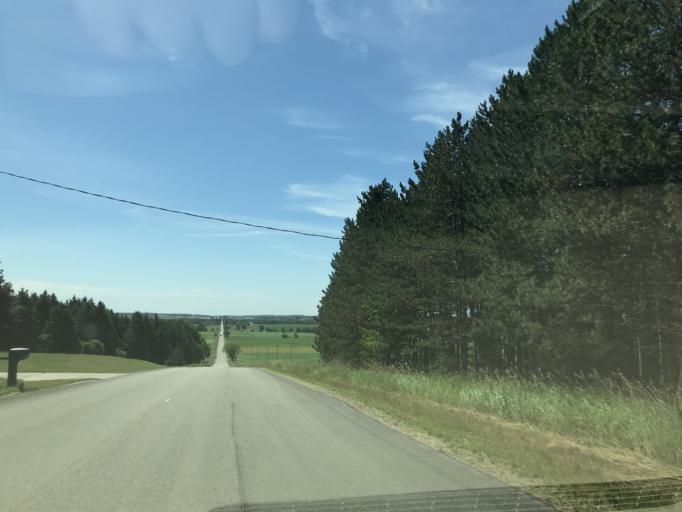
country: US
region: Michigan
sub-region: Missaukee County
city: Lake City
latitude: 44.2928
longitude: -85.0745
